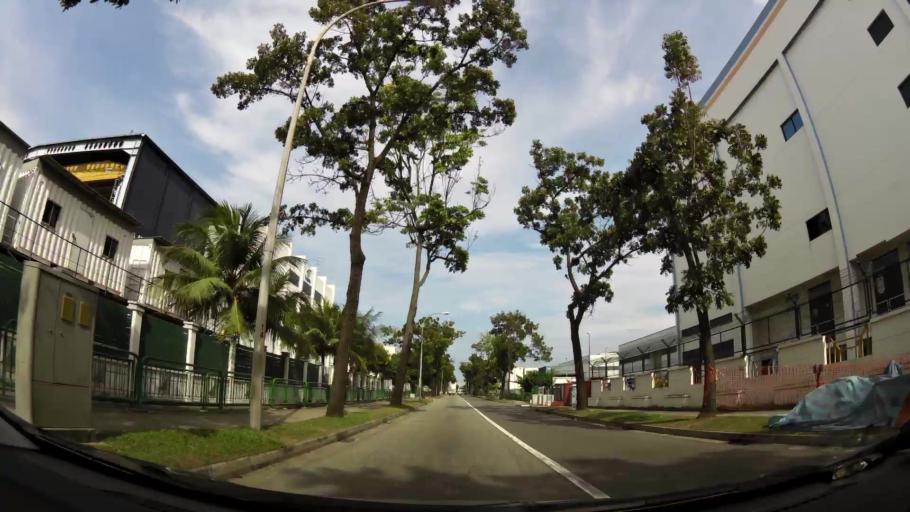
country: MY
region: Johor
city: Johor Bahru
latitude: 1.3177
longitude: 103.6509
